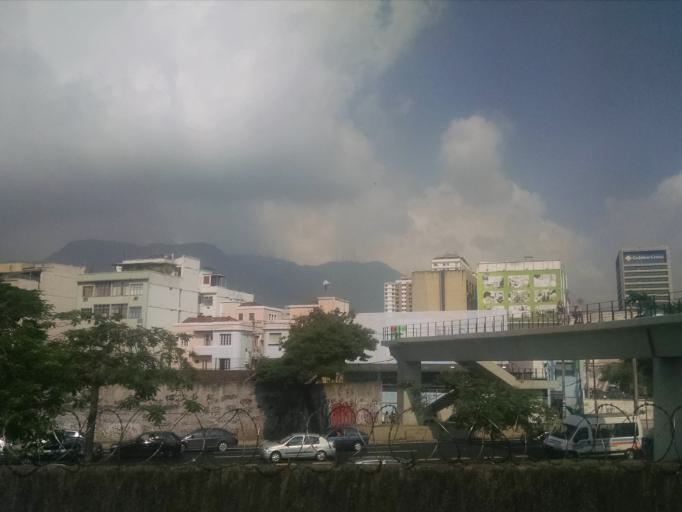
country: BR
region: Rio de Janeiro
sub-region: Rio De Janeiro
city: Rio de Janeiro
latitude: -22.9098
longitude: -43.2198
